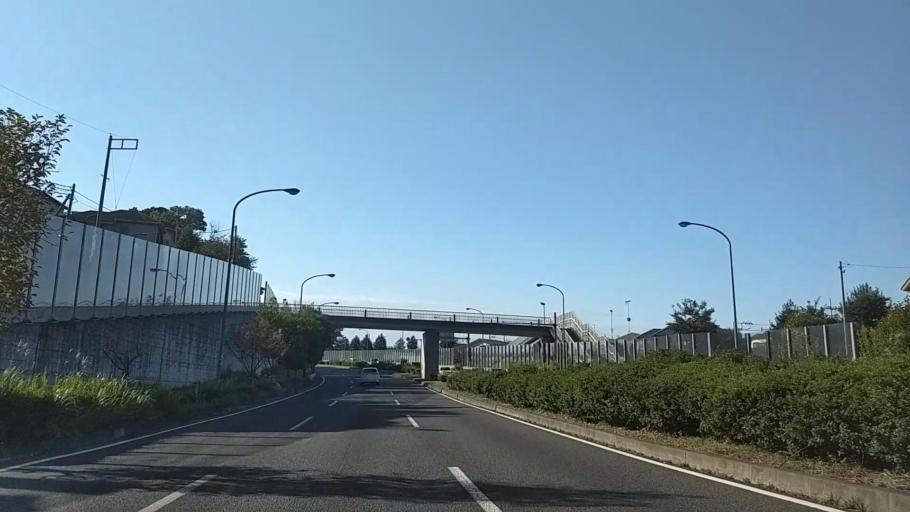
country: JP
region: Kanagawa
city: Yokohama
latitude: 35.4623
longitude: 139.5633
